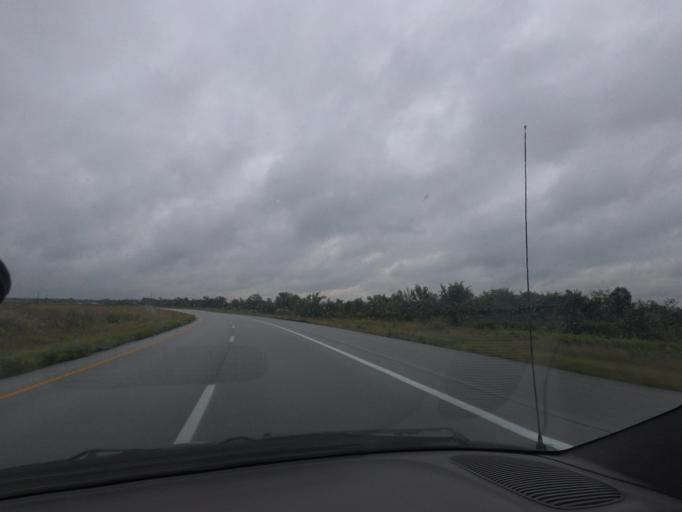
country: US
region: Missouri
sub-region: Marion County
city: Monroe City
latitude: 39.6648
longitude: -91.6780
